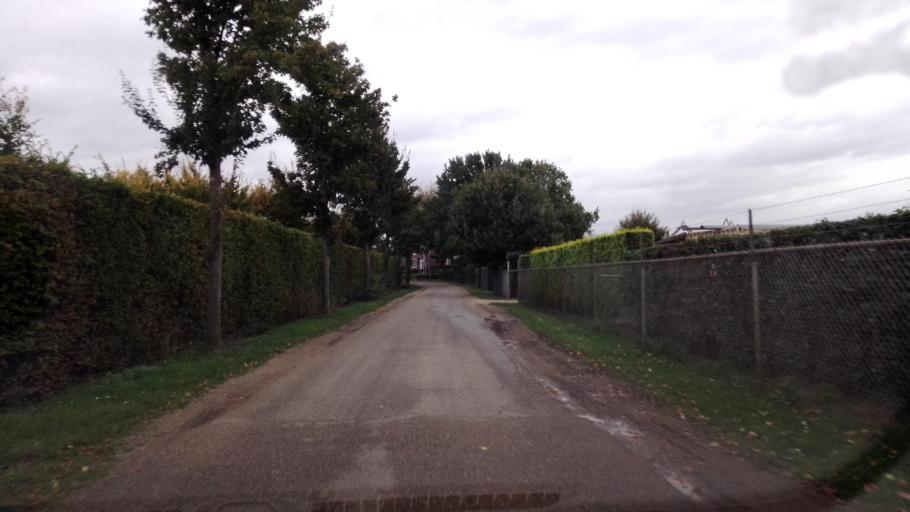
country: NL
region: Limburg
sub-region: Gemeente Venlo
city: Tegelen
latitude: 51.3442
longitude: 6.0952
